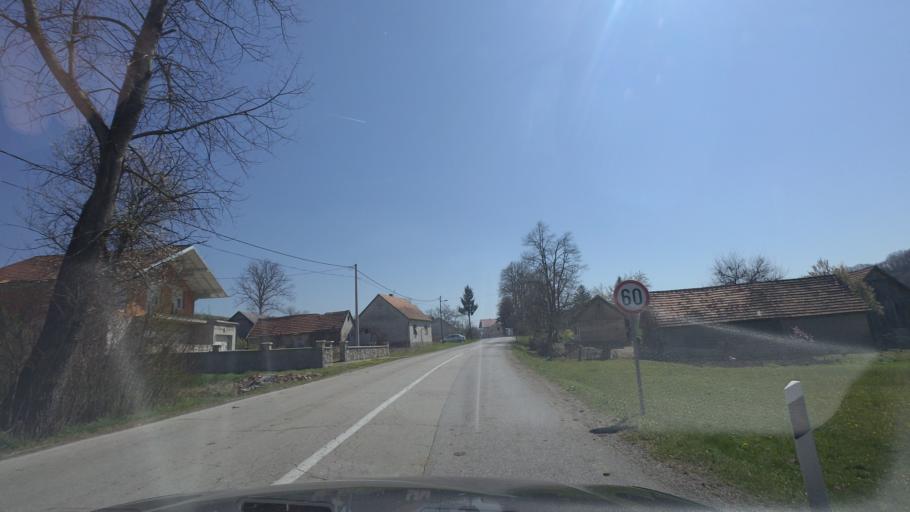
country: HR
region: Karlovacka
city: Vojnic
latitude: 45.3478
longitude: 15.6794
